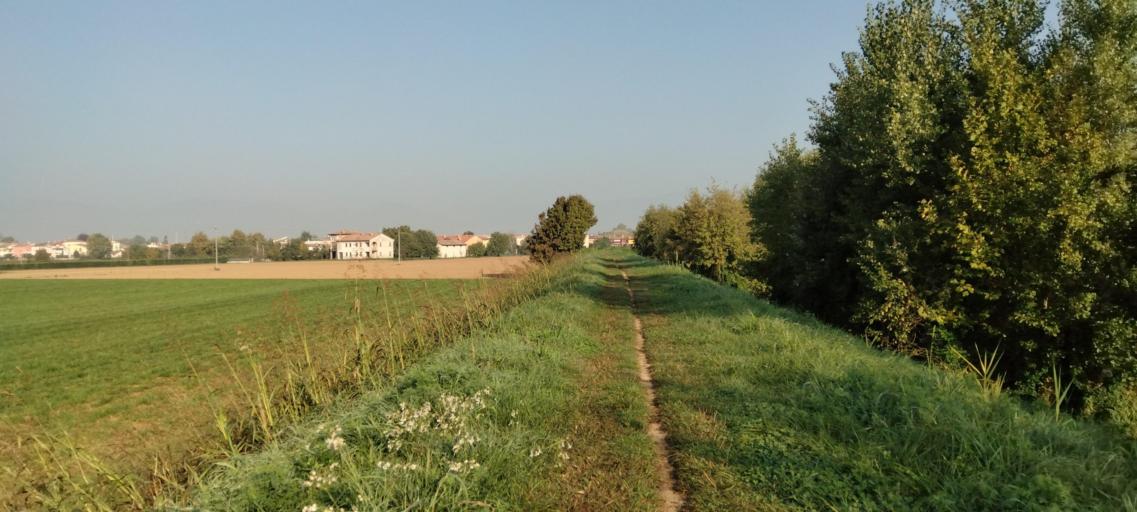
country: IT
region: Veneto
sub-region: Provincia di Vicenza
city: Monticello Conte Otto
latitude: 45.5952
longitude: 11.5368
